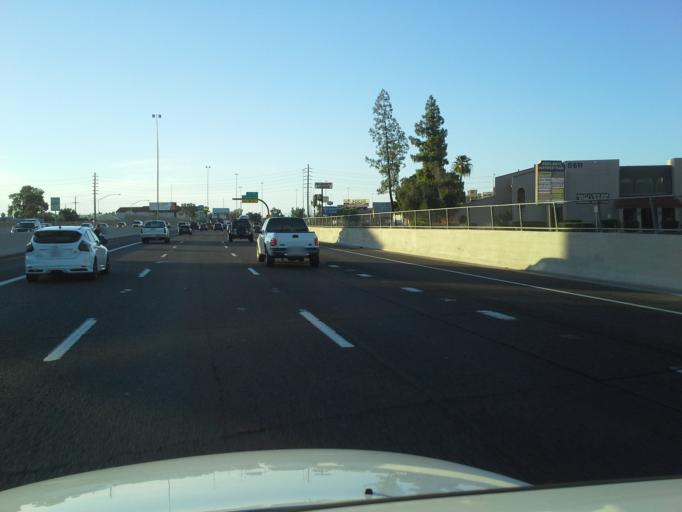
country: US
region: Arizona
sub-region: Maricopa County
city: Glendale
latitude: 33.5617
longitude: -112.1154
